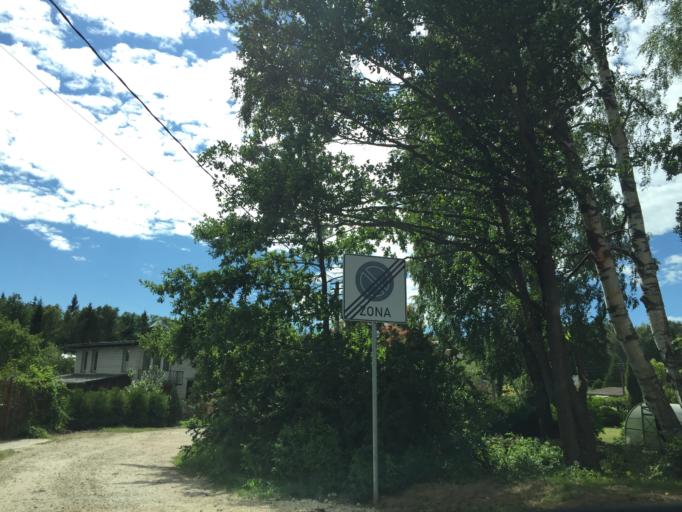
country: LV
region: Carnikava
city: Carnikava
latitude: 57.1178
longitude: 24.2265
